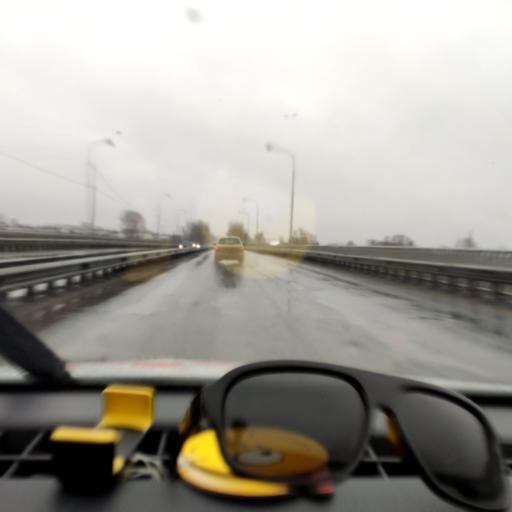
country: RU
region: Bashkortostan
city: Iglino
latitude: 54.7875
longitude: 56.2177
